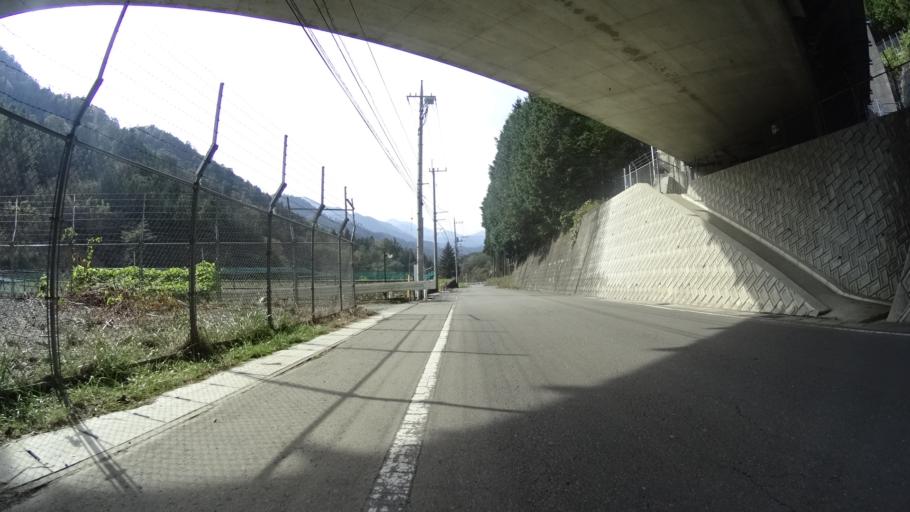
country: JP
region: Yamanashi
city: Otsuki
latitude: 35.5696
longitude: 138.9806
